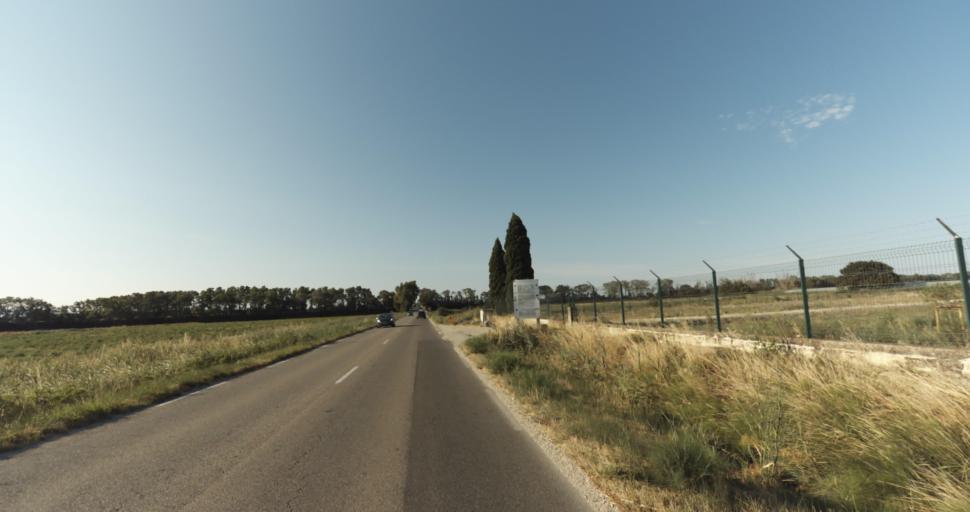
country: FR
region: Provence-Alpes-Cote d'Azur
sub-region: Departement du Vaucluse
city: Sarrians
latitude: 44.0676
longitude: 4.9745
